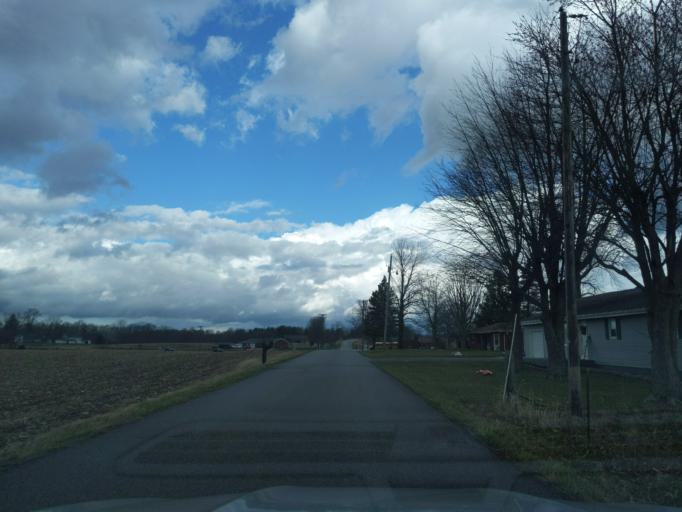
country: US
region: Indiana
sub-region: Decatur County
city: Saint Paul
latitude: 39.4003
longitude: -85.5598
